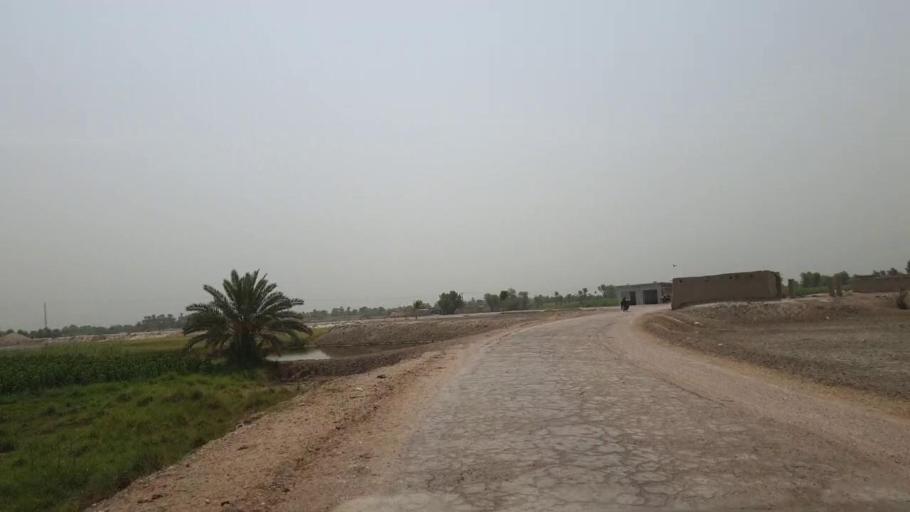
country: PK
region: Sindh
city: Gambat
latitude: 27.4410
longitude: 68.5194
